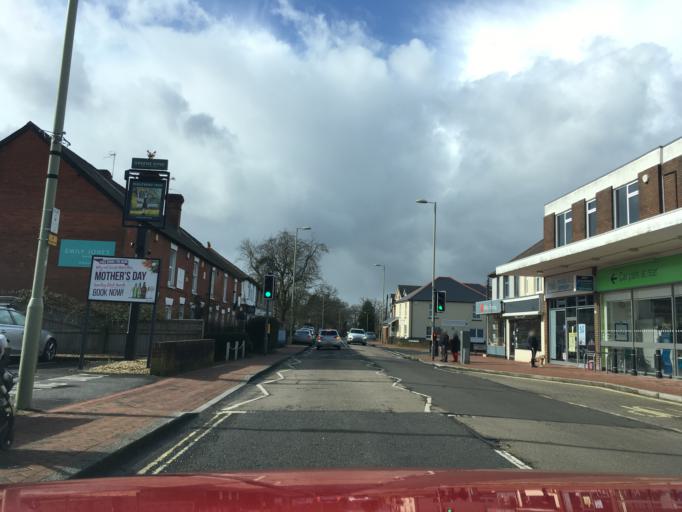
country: GB
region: England
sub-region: Hampshire
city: Chandlers Ford
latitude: 50.9878
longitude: -1.3743
